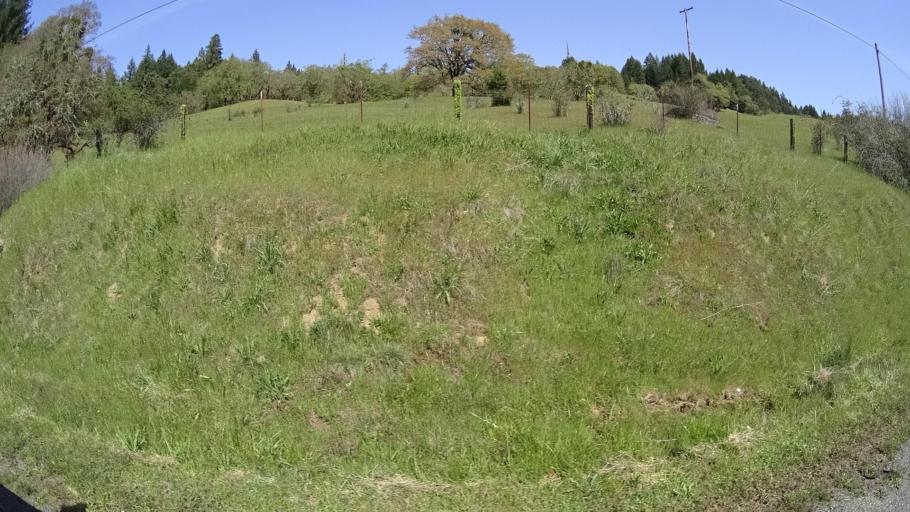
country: US
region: California
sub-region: Humboldt County
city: Redway
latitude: 40.2986
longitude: -123.6528
